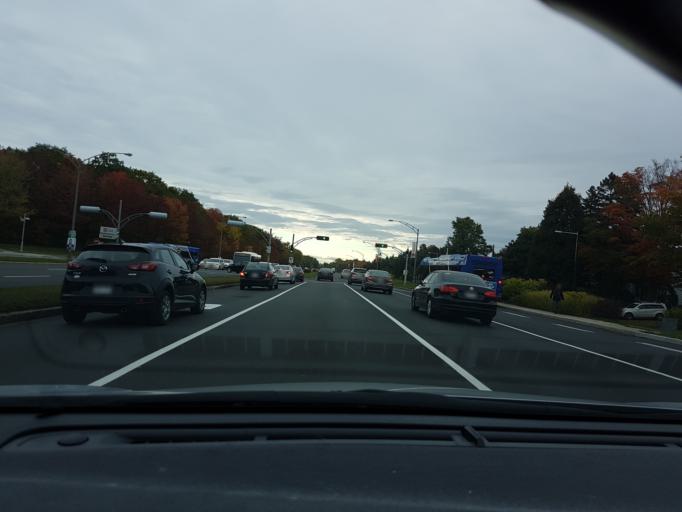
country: CA
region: Quebec
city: Quebec
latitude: 46.7762
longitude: -71.2708
